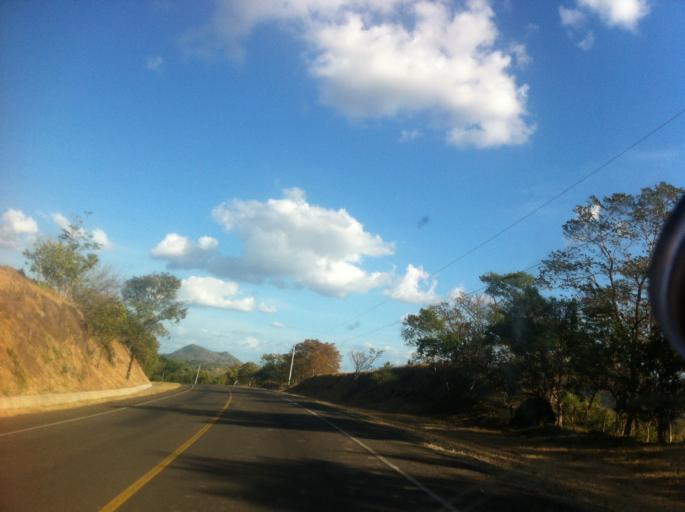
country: NI
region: Chontales
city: Acoyapa
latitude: 11.8718
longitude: -85.0856
